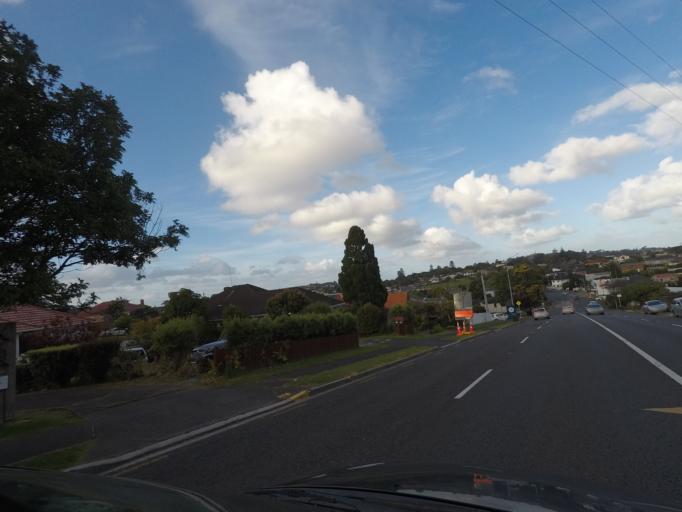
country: NZ
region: Auckland
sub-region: Auckland
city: Auckland
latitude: -36.9211
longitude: 174.7558
